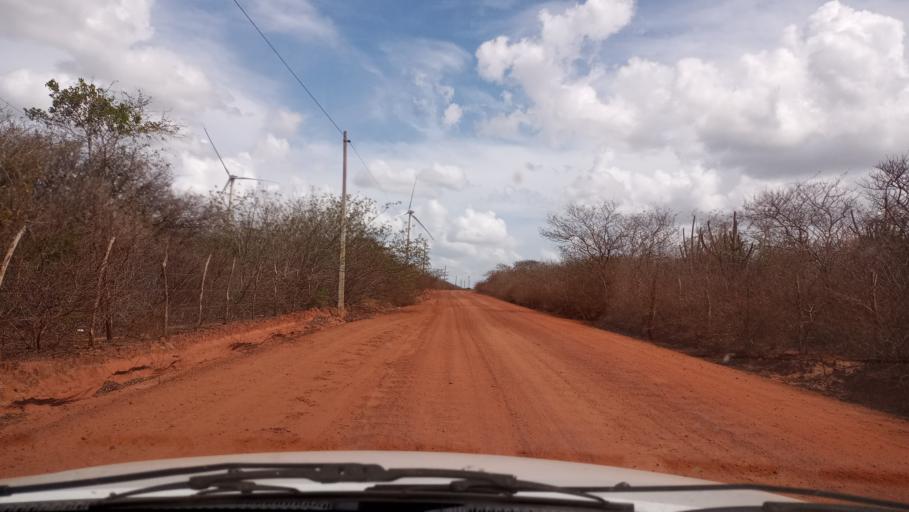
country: BR
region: Rio Grande do Norte
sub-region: Joao Camara
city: Joao Camara
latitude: -5.3870
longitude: -35.8648
